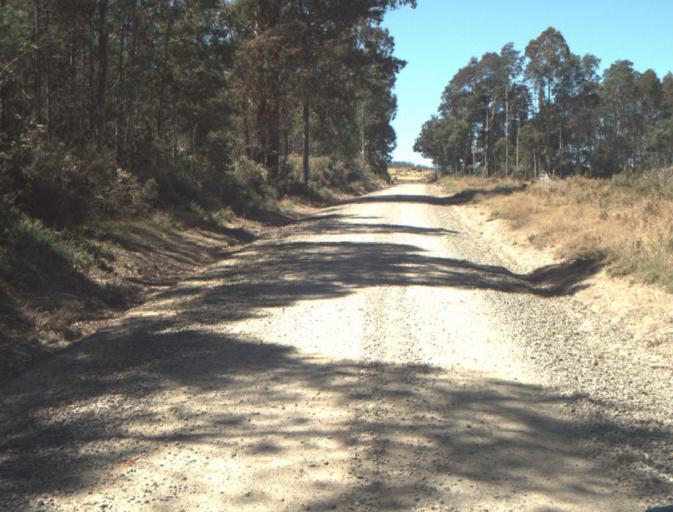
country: AU
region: Tasmania
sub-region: Dorset
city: Scottsdale
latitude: -41.3281
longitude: 147.4848
